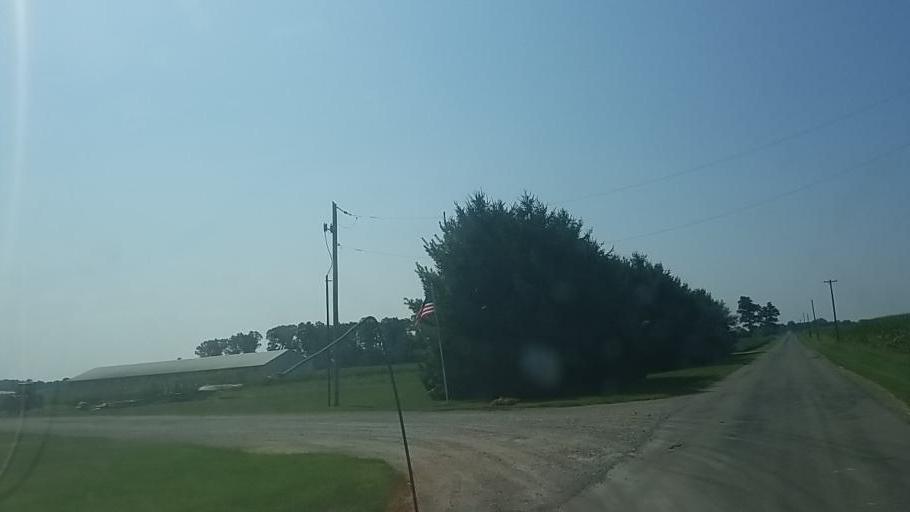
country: US
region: Ohio
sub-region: Marion County
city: Marion
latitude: 40.7161
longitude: -83.1499
